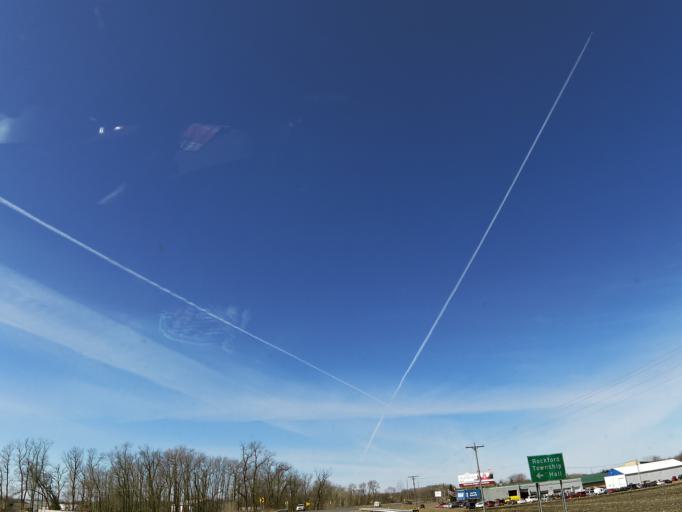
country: US
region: Minnesota
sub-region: Wright County
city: Delano
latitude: 45.1157
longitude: -93.8047
